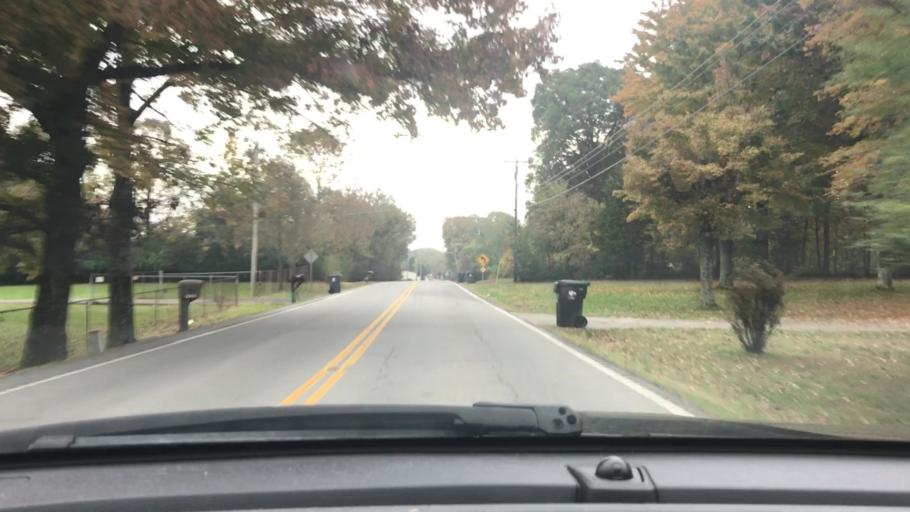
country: US
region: Tennessee
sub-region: Sumner County
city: Millersville
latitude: 36.4075
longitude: -86.6936
